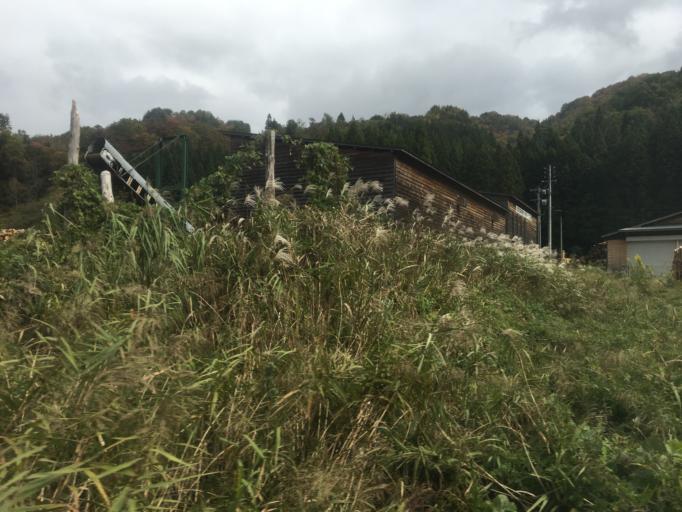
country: JP
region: Yamagata
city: Nagai
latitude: 38.0531
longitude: 139.7957
